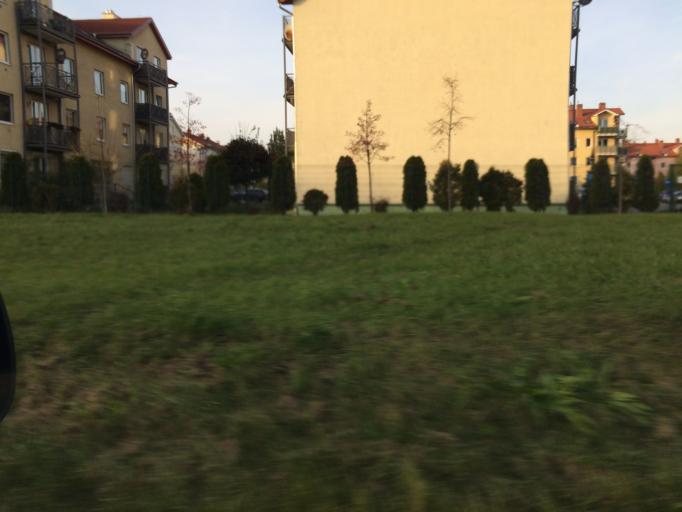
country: PL
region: Opole Voivodeship
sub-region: Powiat opolski
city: Opole
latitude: 50.6754
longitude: 17.9728
